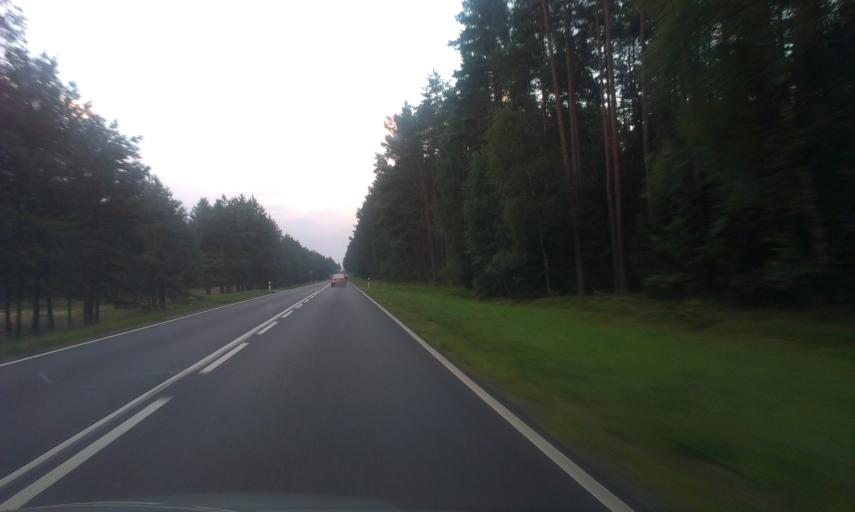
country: PL
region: West Pomeranian Voivodeship
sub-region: Powiat koszalinski
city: Sianow
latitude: 54.1029
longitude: 16.3452
